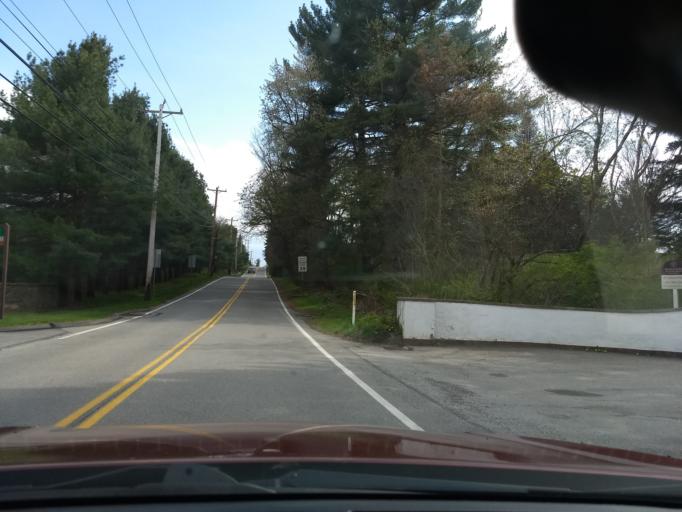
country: US
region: Pennsylvania
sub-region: Allegheny County
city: Fox Chapel
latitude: 40.5510
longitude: -79.8774
